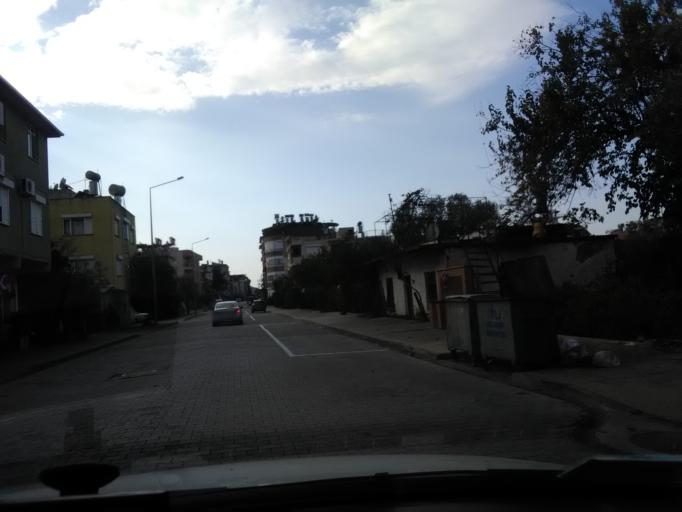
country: TR
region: Antalya
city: Gazipasa
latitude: 36.2695
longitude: 32.3246
